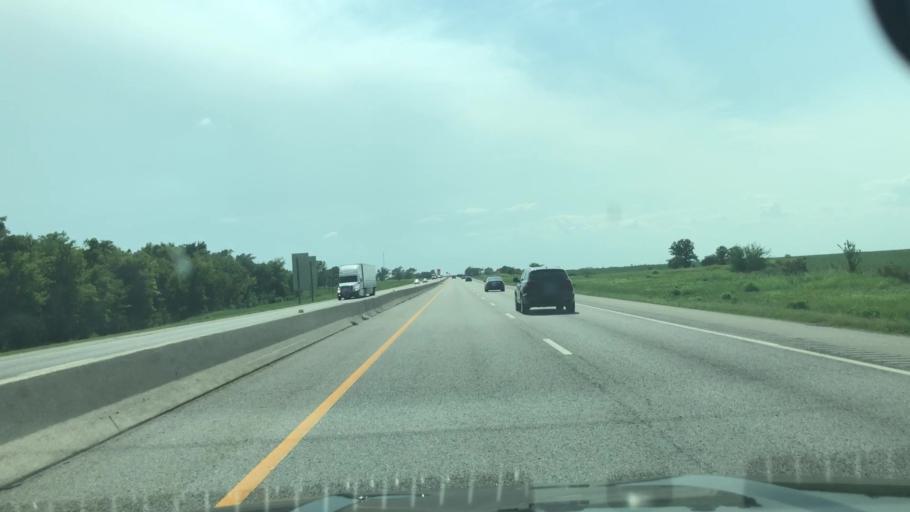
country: US
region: Oklahoma
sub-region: Ottawa County
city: Afton
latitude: 36.7107
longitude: -94.9680
